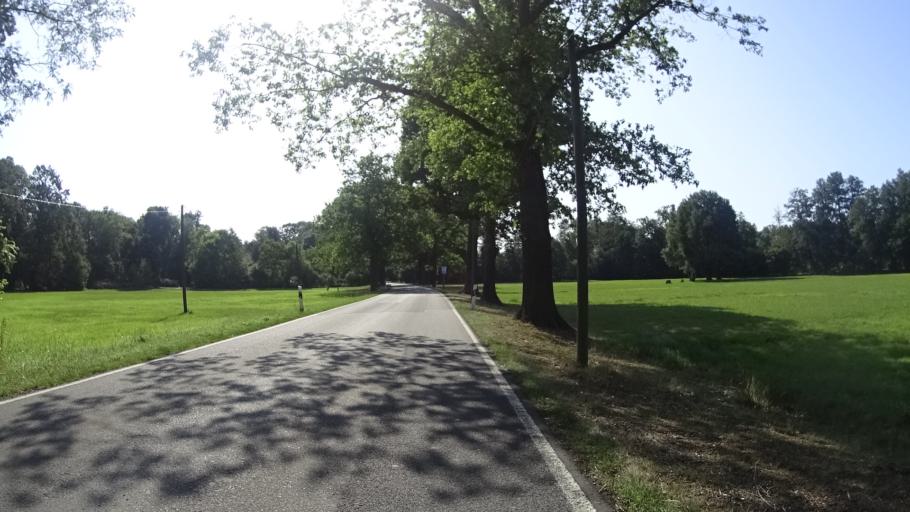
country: DE
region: Brandenburg
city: Straupitz
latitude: 51.8719
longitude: 14.1184
